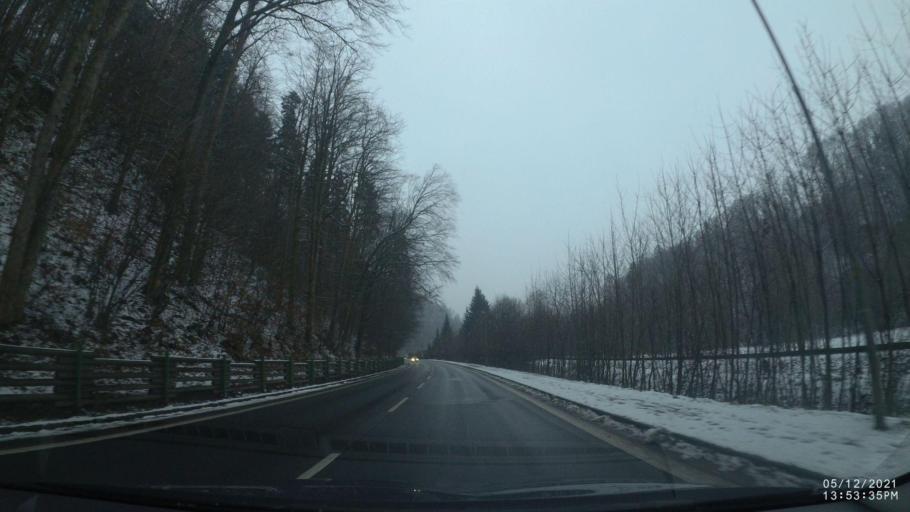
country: CZ
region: Kralovehradecky
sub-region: Okres Nachod
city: Police nad Metuji
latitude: 50.5162
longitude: 16.2118
